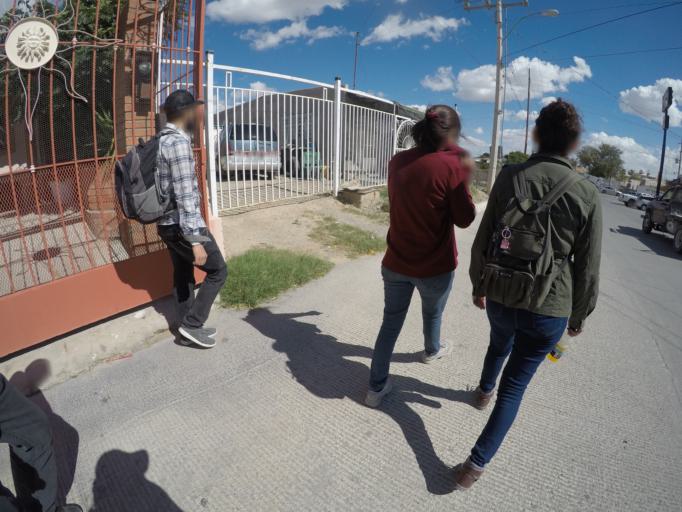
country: MX
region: Chihuahua
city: Ciudad Juarez
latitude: 31.6923
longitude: -106.4817
